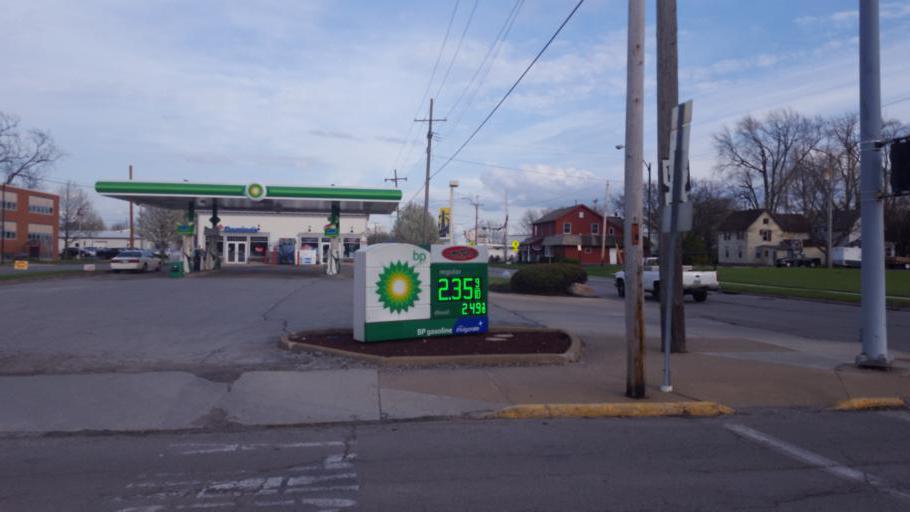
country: US
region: Ohio
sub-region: Erie County
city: Huron
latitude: 41.3913
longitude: -82.5580
